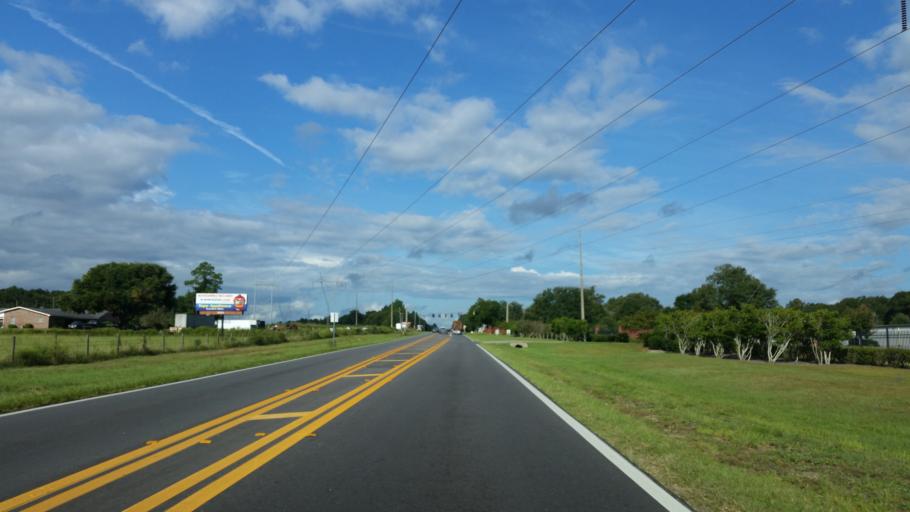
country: US
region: Florida
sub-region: Santa Rosa County
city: Wallace
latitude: 30.6474
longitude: -87.1450
